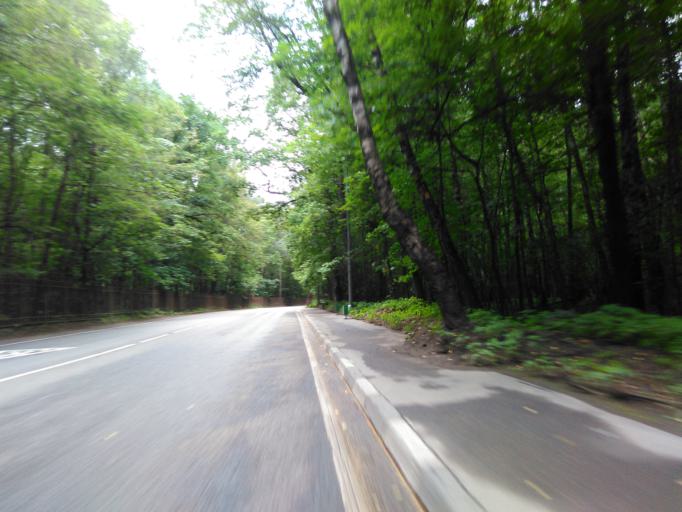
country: RU
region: Moscow
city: Rostokino
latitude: 55.8253
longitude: 37.6919
